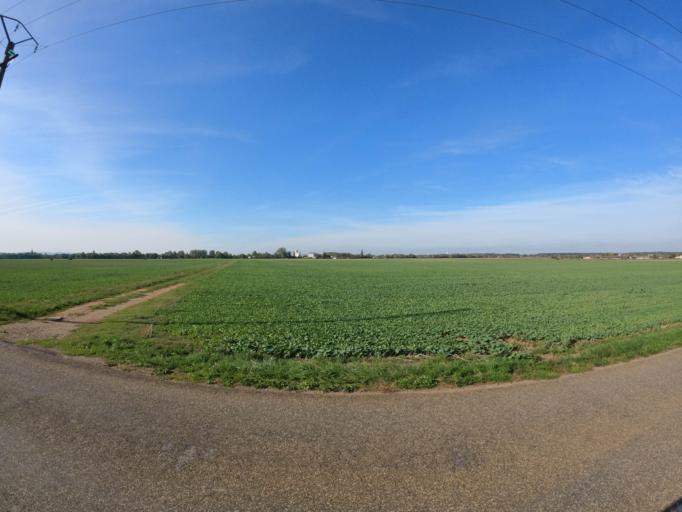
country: FR
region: Franche-Comte
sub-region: Departement du Jura
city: Bletterans
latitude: 46.7559
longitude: 5.4822
